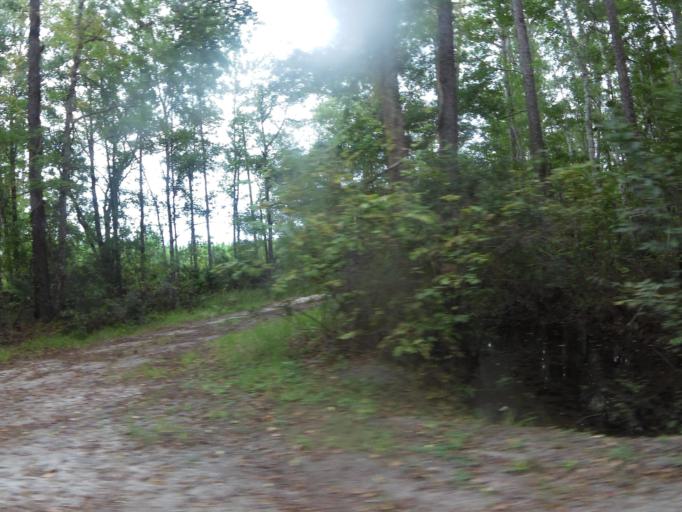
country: US
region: Florida
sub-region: Flagler County
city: Palm Coast
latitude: 29.6348
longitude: -81.3717
